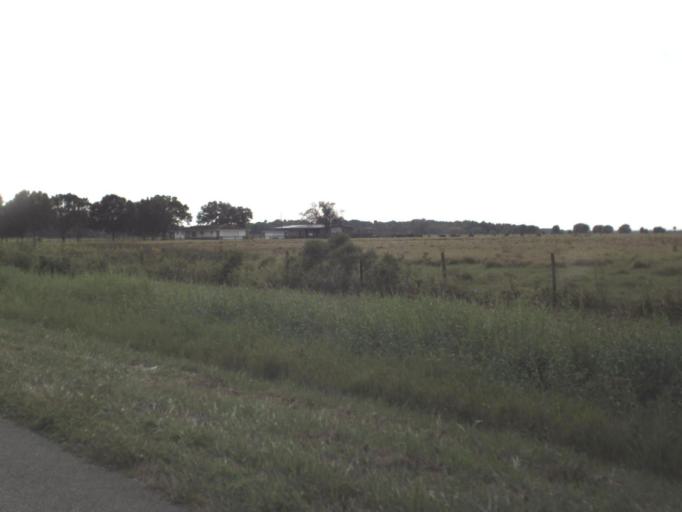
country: US
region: Florida
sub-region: Okeechobee County
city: Cypress Quarters
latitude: 27.4056
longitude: -80.8146
